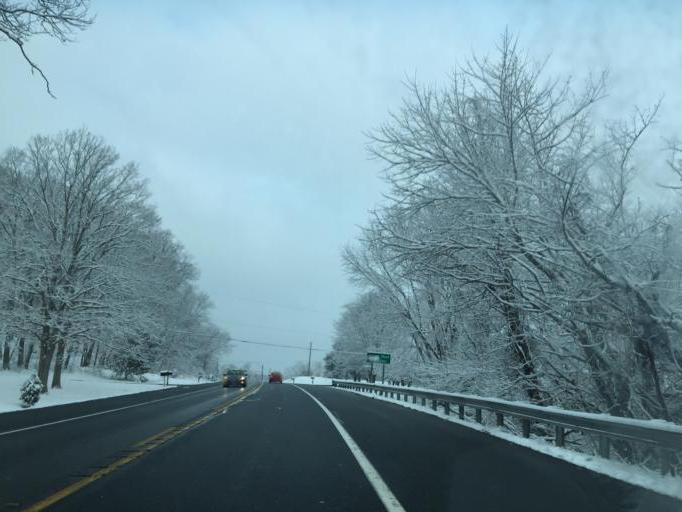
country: US
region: Maryland
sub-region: Harford County
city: Joppatowne
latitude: 39.4637
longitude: -76.3664
